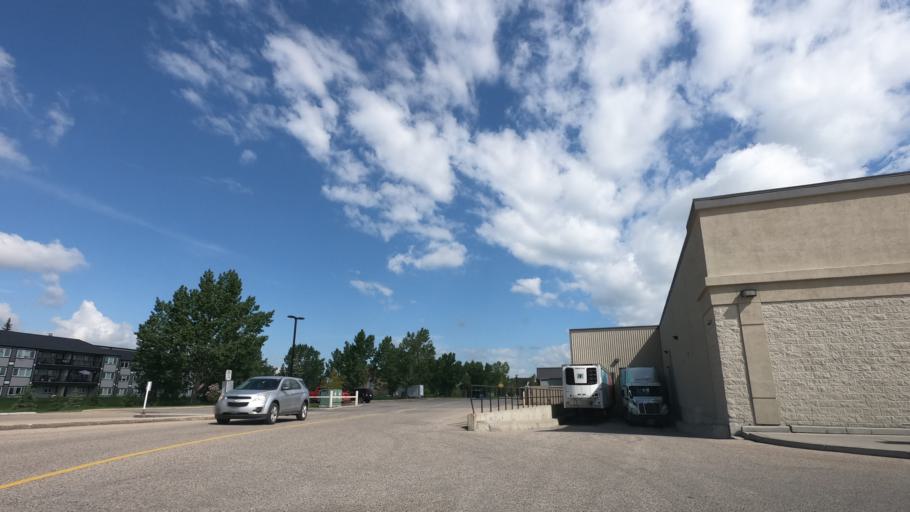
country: CA
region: Alberta
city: Airdrie
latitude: 51.2874
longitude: -114.0156
